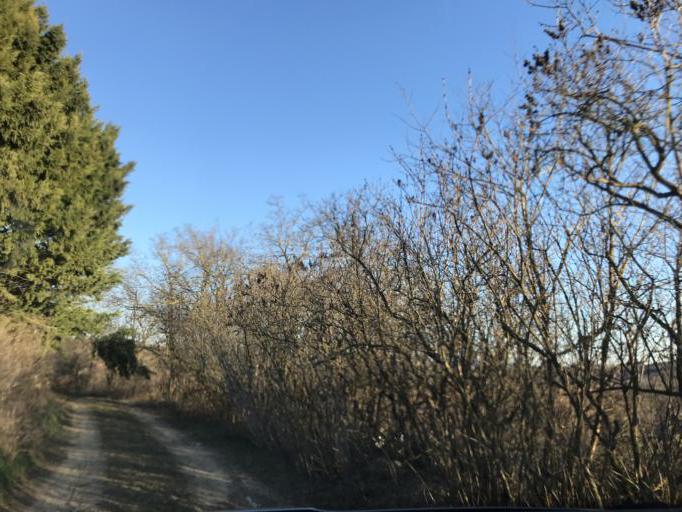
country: HU
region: Komarom-Esztergom
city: Csolnok
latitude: 47.6426
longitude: 18.7420
